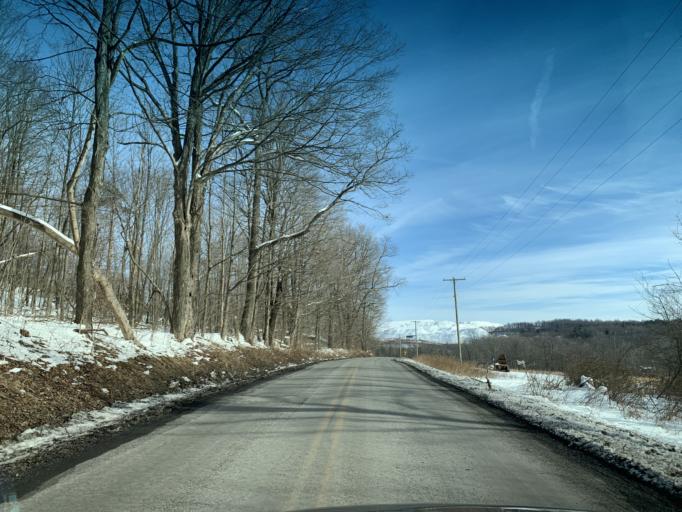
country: US
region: Maryland
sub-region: Allegany County
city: Frostburg
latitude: 39.6213
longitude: -78.9355
